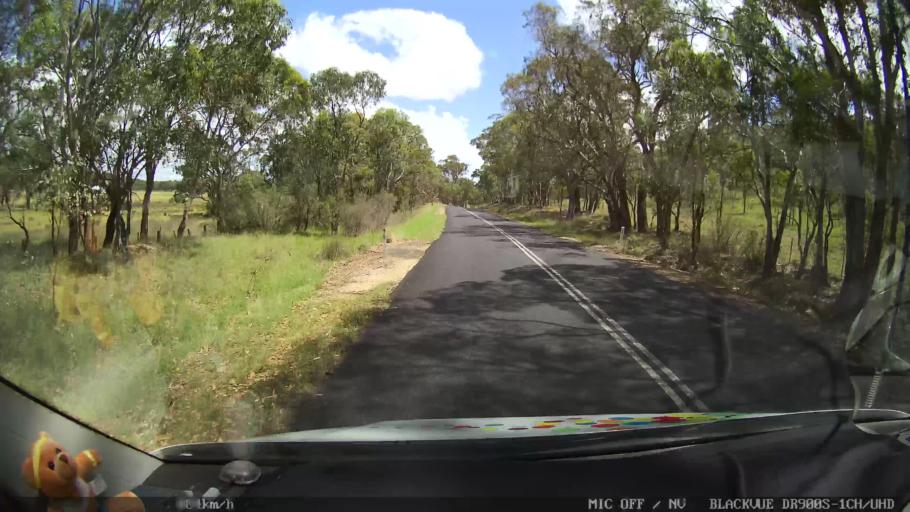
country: AU
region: New South Wales
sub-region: Glen Innes Severn
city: Glen Innes
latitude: -29.5316
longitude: 151.6736
